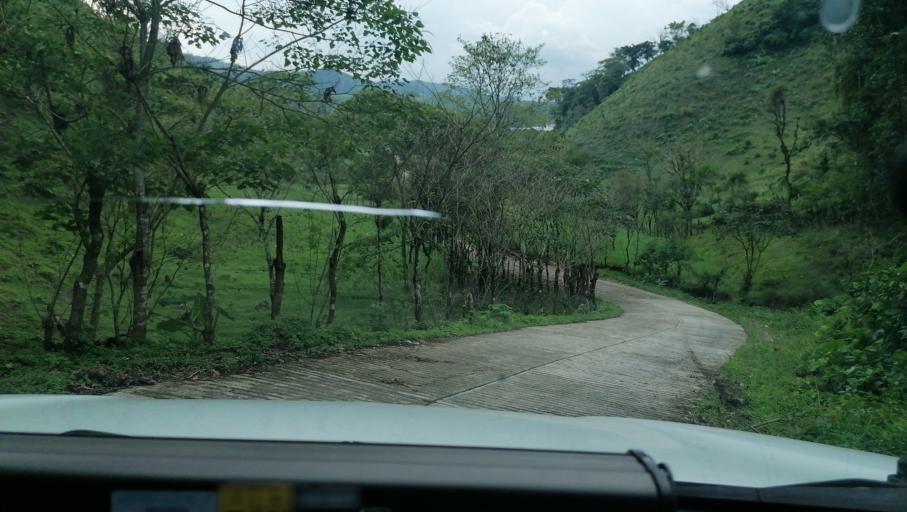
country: MX
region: Chiapas
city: Ixtacomitan
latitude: 17.3399
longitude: -93.1230
